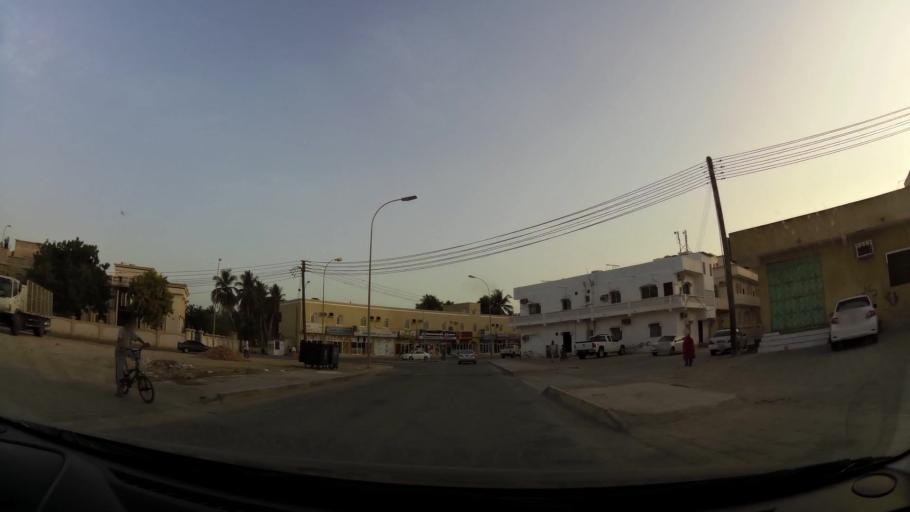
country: OM
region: Zufar
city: Salalah
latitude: 17.0181
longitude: 54.1217
